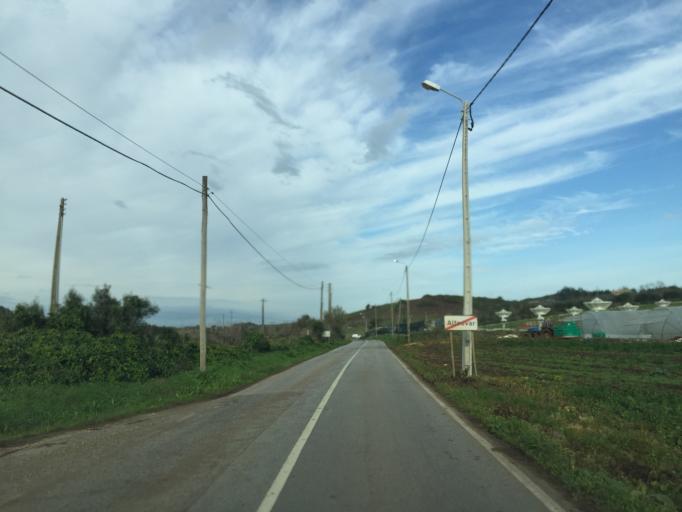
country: PT
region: Lisbon
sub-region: Sintra
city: Almargem
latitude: 38.8686
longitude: -9.2847
